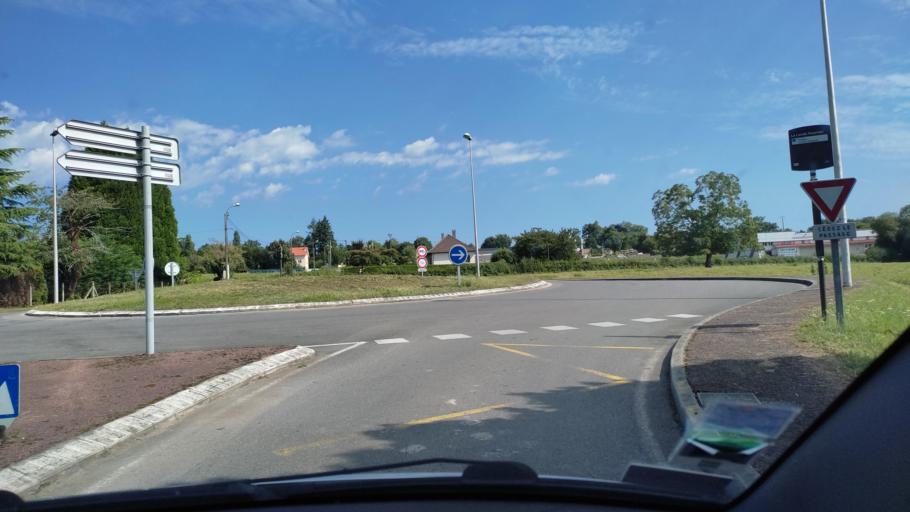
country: FR
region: Limousin
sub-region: Departement de la Haute-Vienne
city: Isle
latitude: 45.8347
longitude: 1.1942
